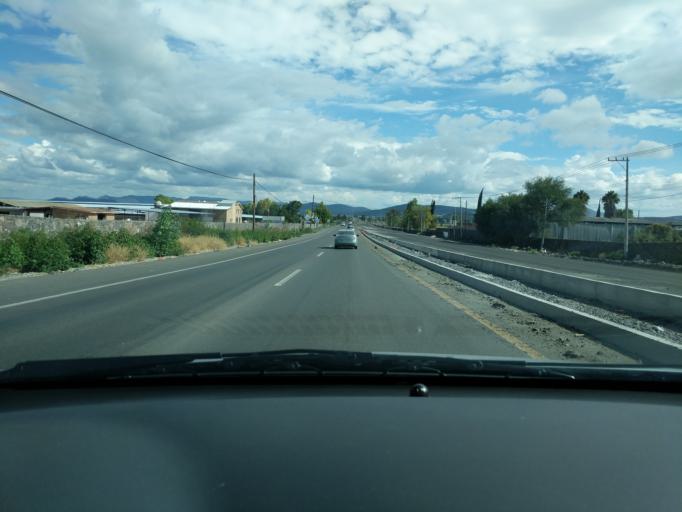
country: MX
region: Queretaro
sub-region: El Marques
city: Paseos del Marques
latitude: 20.5996
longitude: -100.2466
